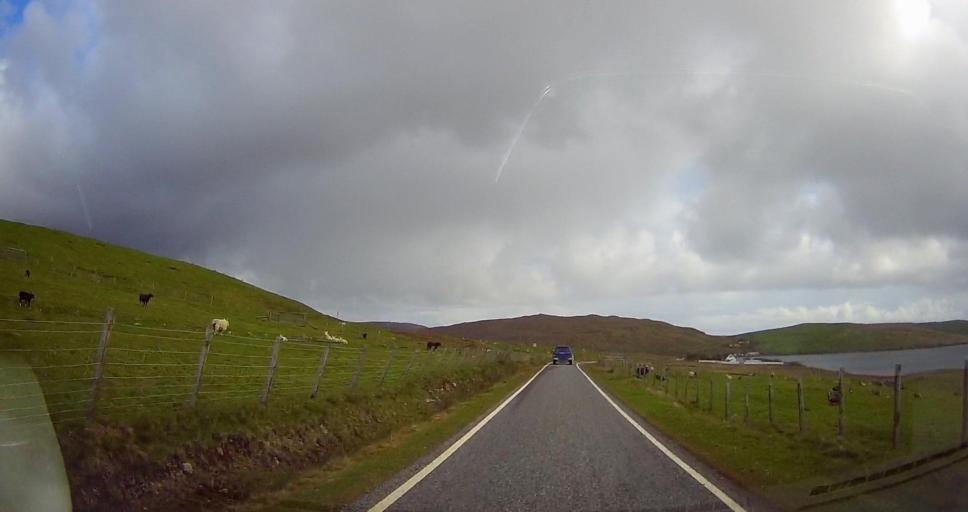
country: GB
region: Scotland
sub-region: Shetland Islands
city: Lerwick
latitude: 60.5321
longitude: -1.3622
